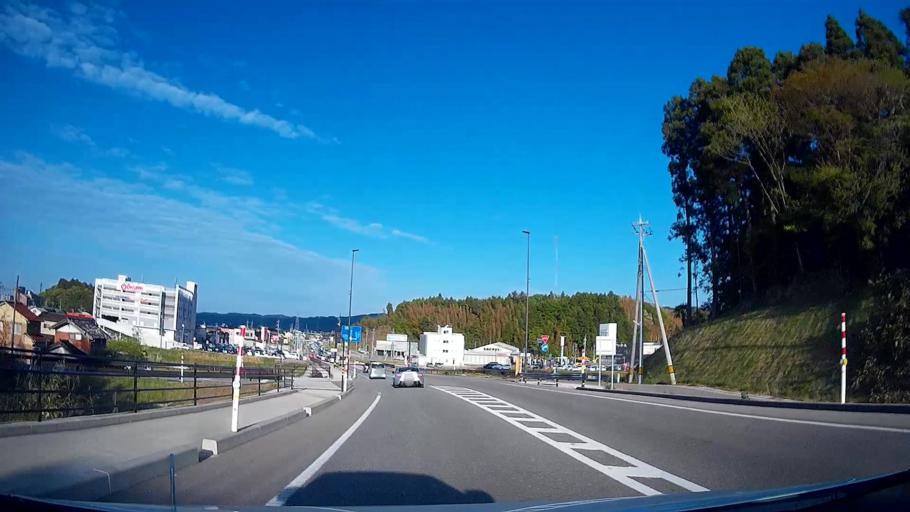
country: JP
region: Ishikawa
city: Nanao
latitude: 37.0344
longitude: 136.9499
